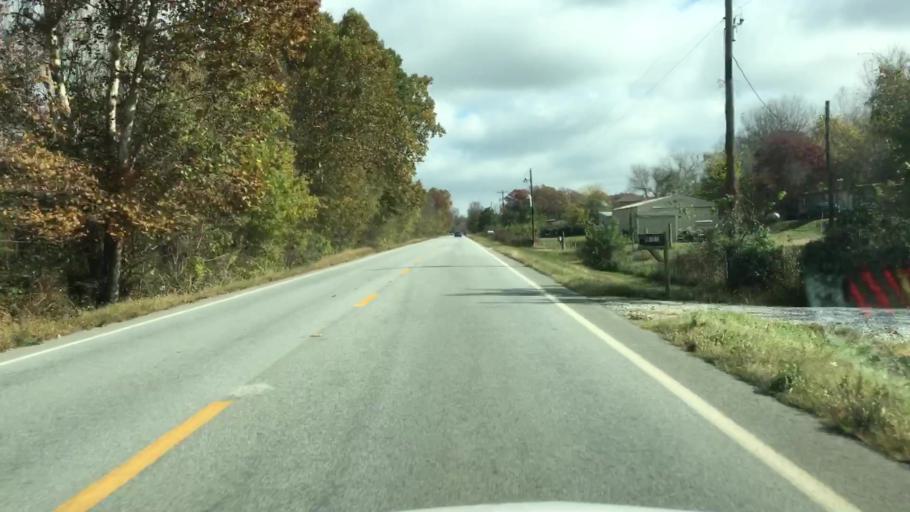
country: US
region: Arkansas
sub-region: Benton County
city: Gentry
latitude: 36.2578
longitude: -94.3896
